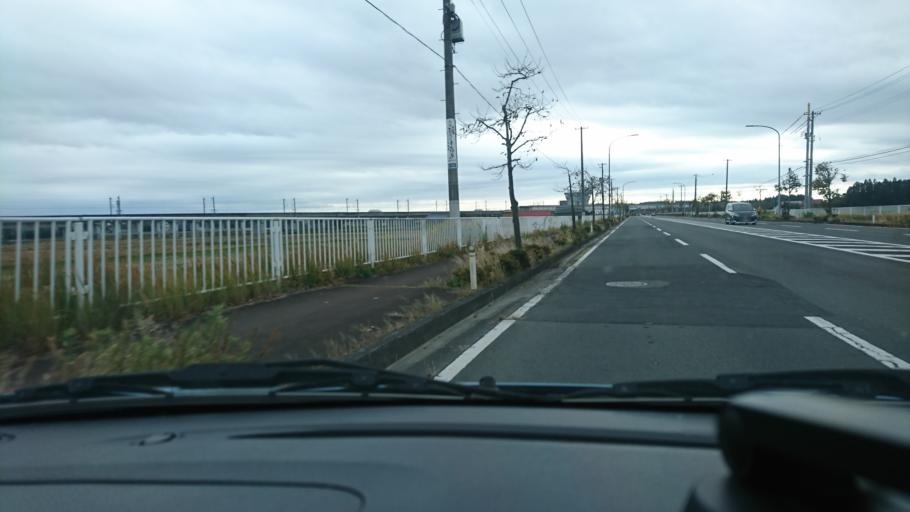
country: JP
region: Iwate
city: Ichinoseki
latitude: 38.7551
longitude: 141.0715
